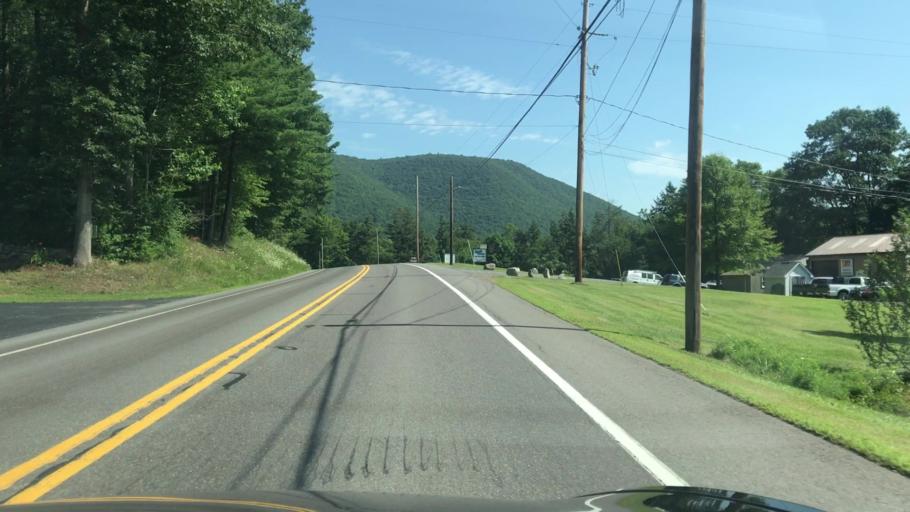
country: US
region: Pennsylvania
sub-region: Lycoming County
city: Garden View
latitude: 41.4035
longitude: -77.0447
